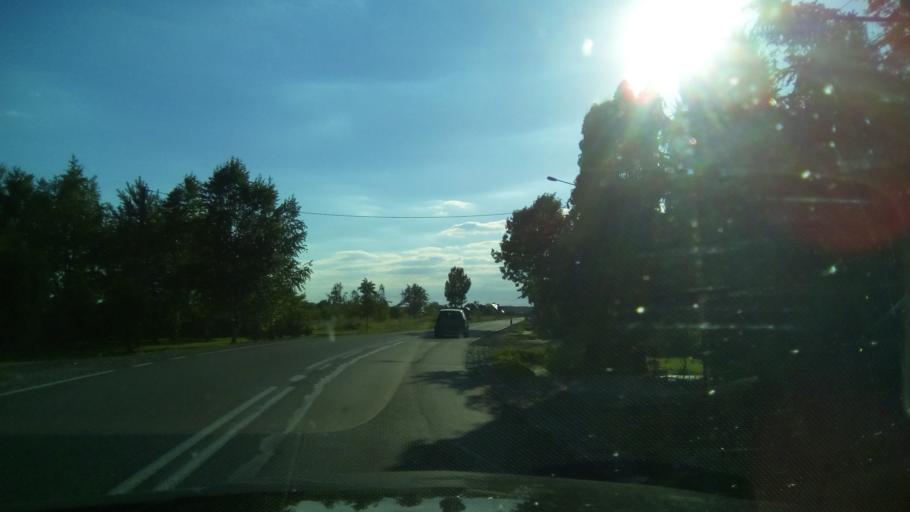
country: PL
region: Masovian Voivodeship
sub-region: Powiat radomski
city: Jastrzebia
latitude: 51.6174
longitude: 21.2135
